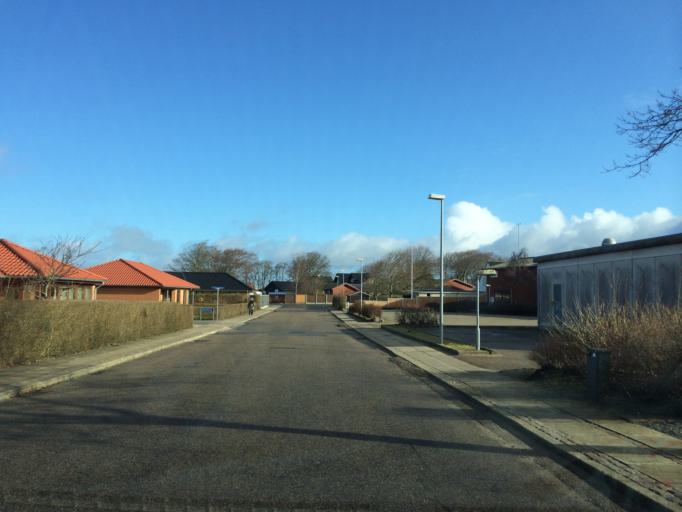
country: DK
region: Central Jutland
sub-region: Holstebro Kommune
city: Ulfborg
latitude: 56.2731
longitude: 8.3191
